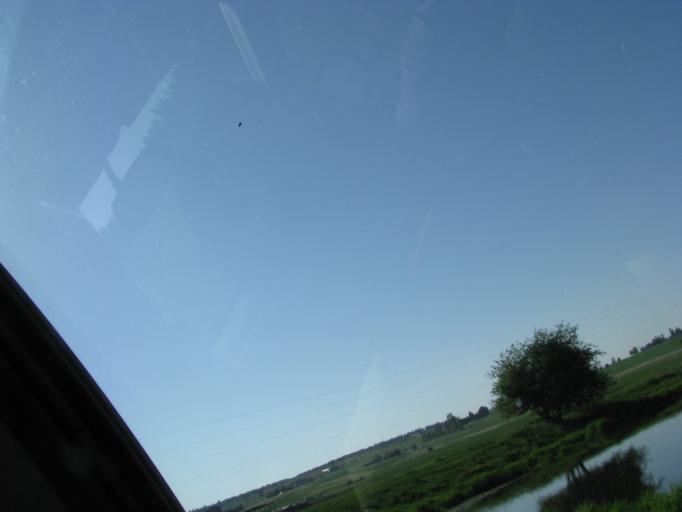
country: US
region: Washington
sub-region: Spokane County
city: Liberty Lake
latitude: 47.6278
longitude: -117.1414
